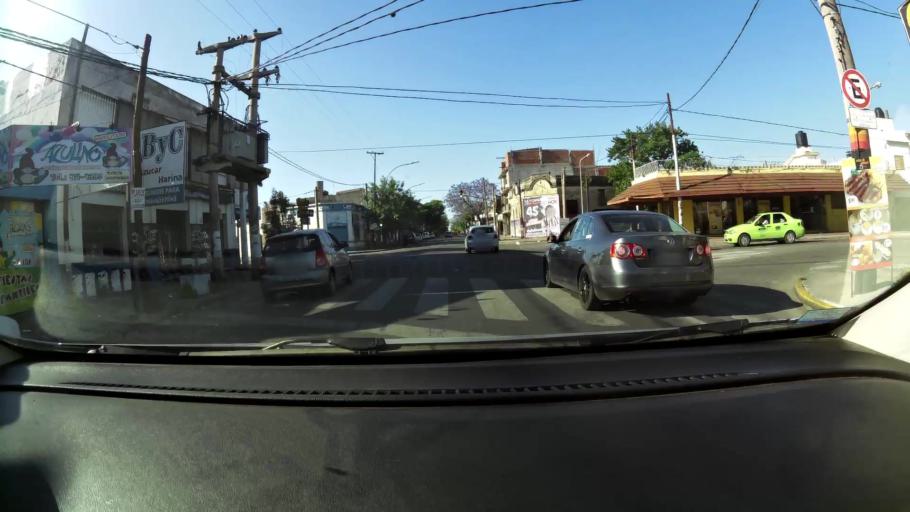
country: AR
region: Cordoba
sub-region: Departamento de Capital
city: Cordoba
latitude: -31.3902
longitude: -64.1759
